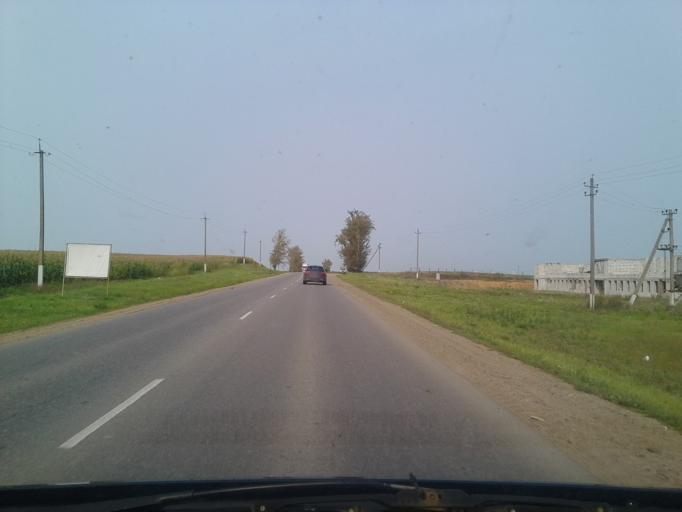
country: BY
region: Minsk
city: Hatava
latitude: 53.7865
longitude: 27.6529
